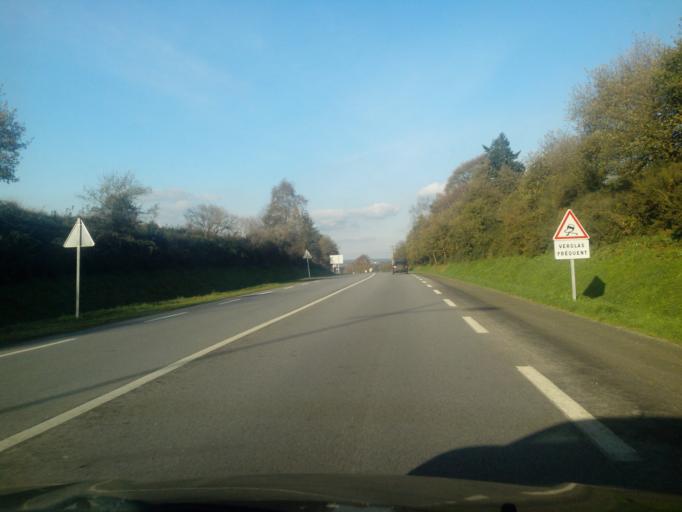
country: FR
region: Brittany
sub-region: Departement du Morbihan
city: Ploermel
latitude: 47.9467
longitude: -2.3963
